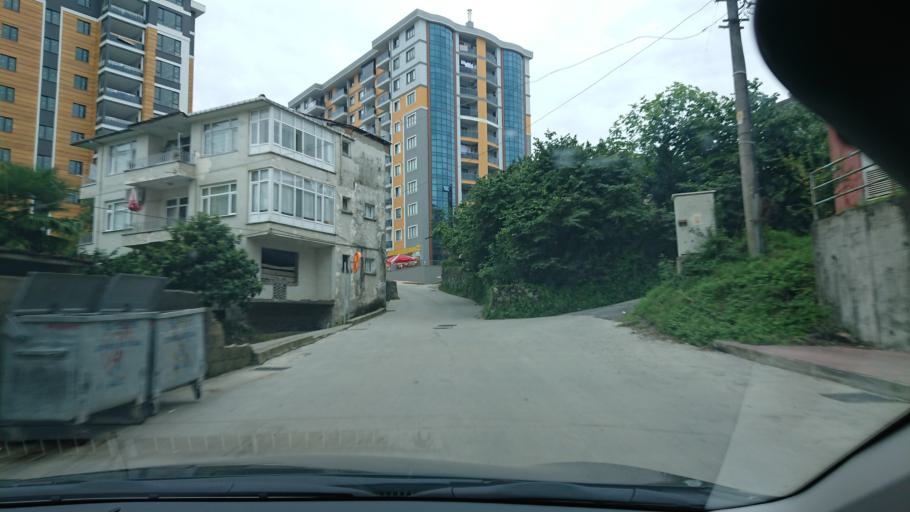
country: TR
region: Rize
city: Rize
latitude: 41.0193
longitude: 40.5122
